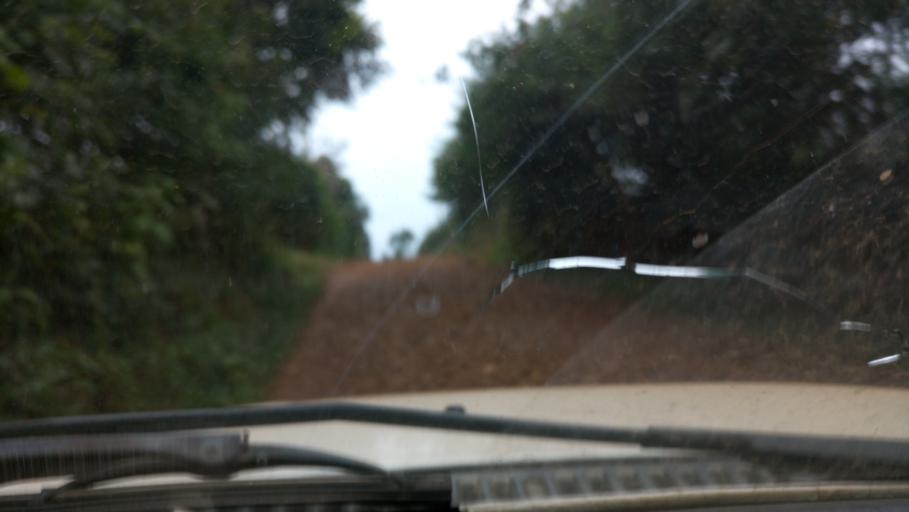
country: KE
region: Murang'a District
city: Kangema
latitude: -0.6819
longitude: 36.9465
